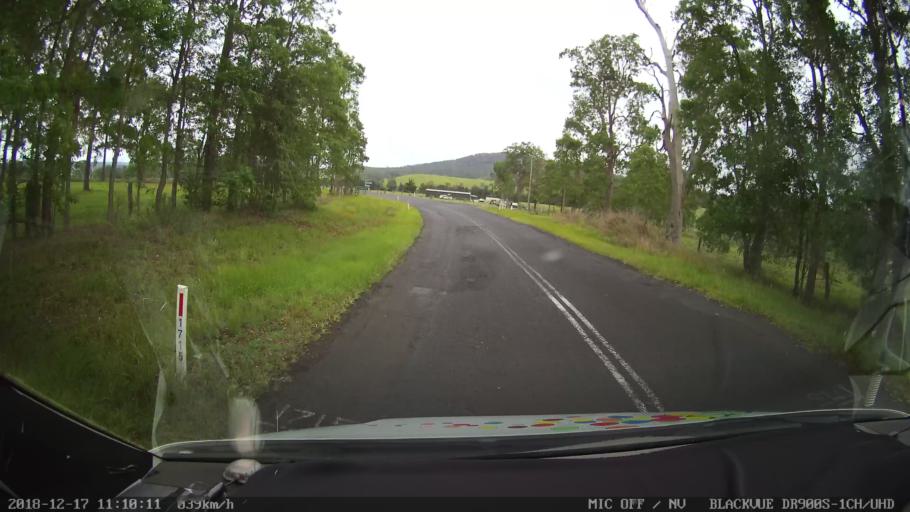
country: AU
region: New South Wales
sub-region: Kyogle
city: Kyogle
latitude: -28.7503
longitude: 152.6520
